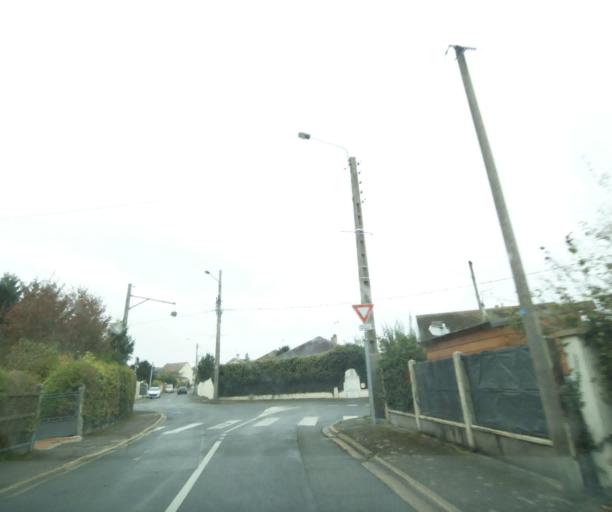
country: FR
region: Centre
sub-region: Departement d'Eure-et-Loir
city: Vernouillet
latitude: 48.7203
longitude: 1.3619
